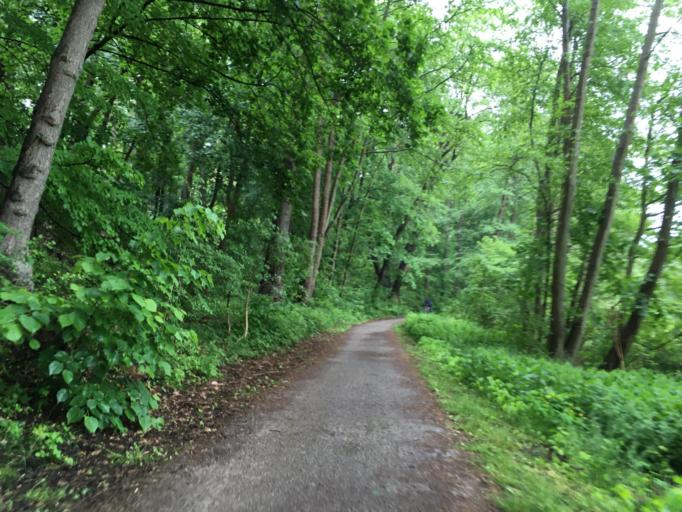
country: DE
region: Brandenburg
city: Eberswalde
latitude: 52.8425
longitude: 13.7545
